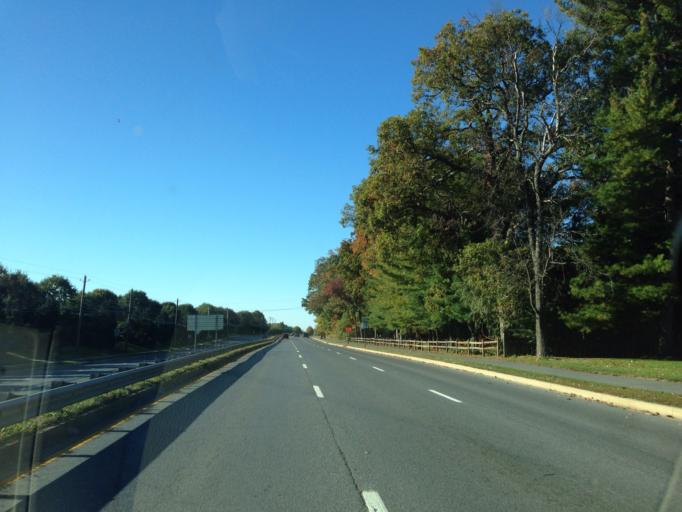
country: US
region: Maryland
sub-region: Montgomery County
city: Germantown
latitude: 39.2094
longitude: -77.2403
